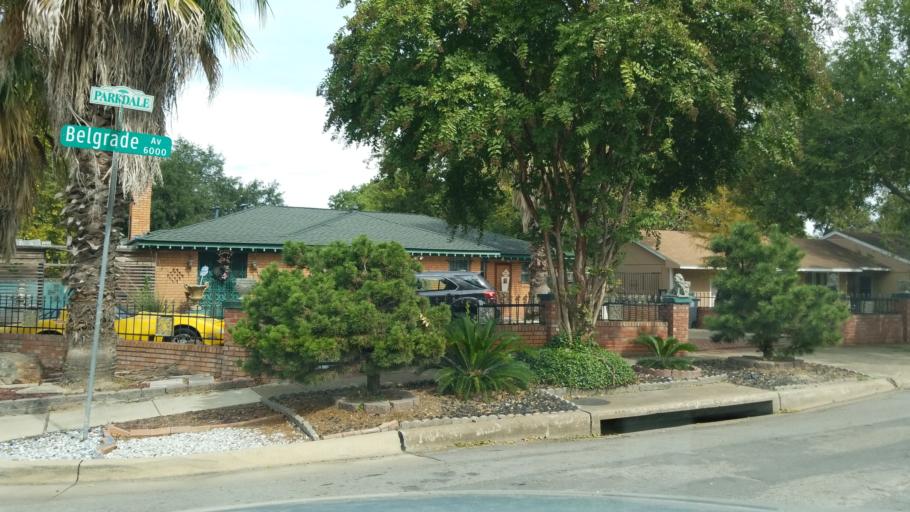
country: US
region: Texas
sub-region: Dallas County
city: Dallas
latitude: 32.7748
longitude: -96.7179
